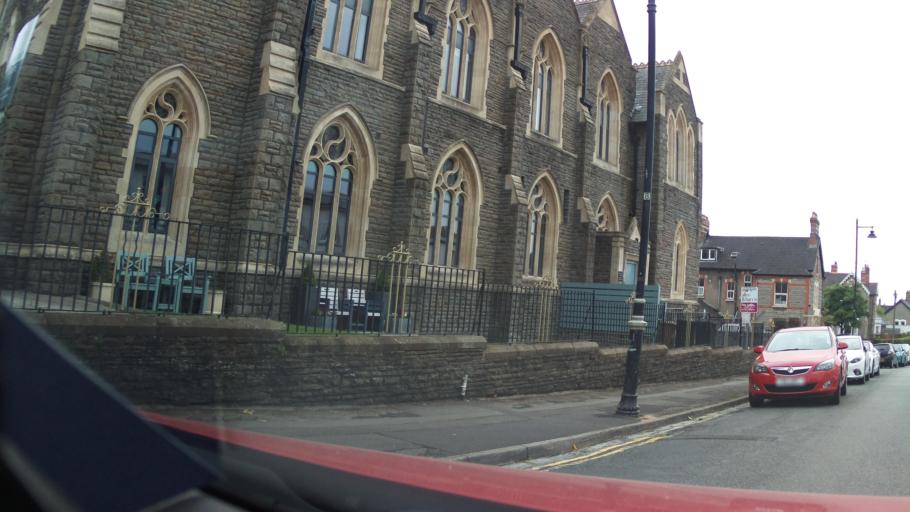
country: GB
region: Wales
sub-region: Vale of Glamorgan
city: Penarth
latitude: 51.4406
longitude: -3.1722
